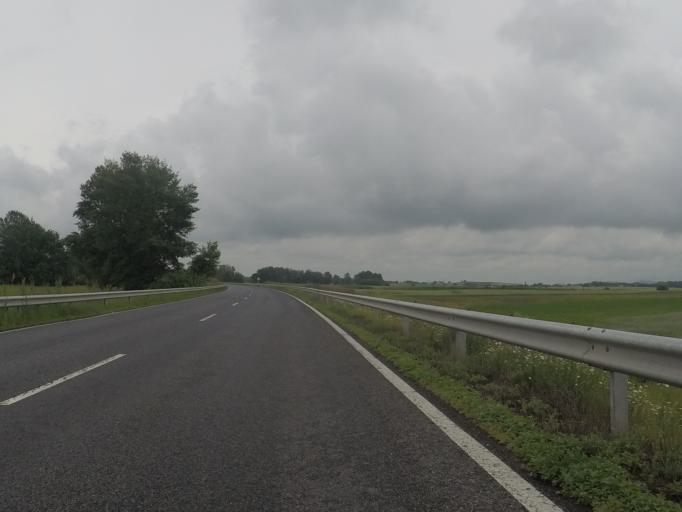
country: HU
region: Gyor-Moson-Sopron
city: Gyorujbarat
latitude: 47.6321
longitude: 17.6635
